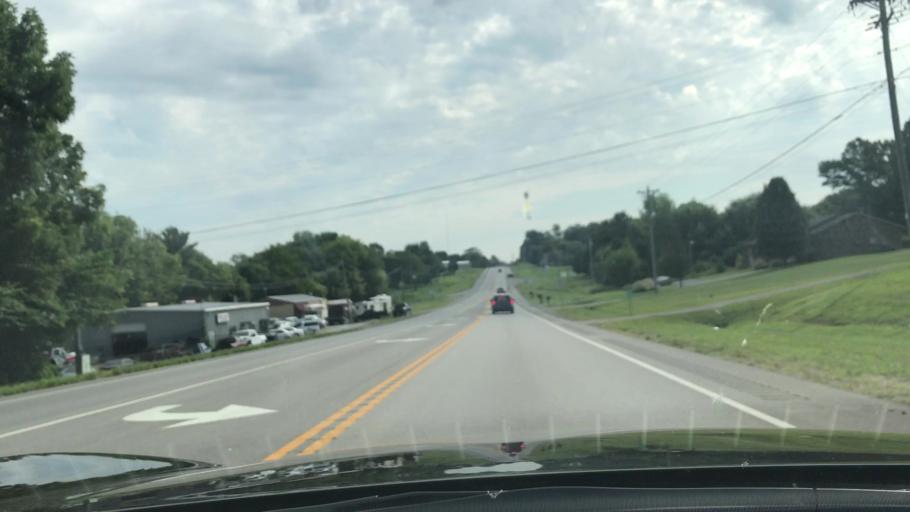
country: US
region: Kentucky
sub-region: Taylor County
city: Campbellsville
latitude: 37.3273
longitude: -85.3902
